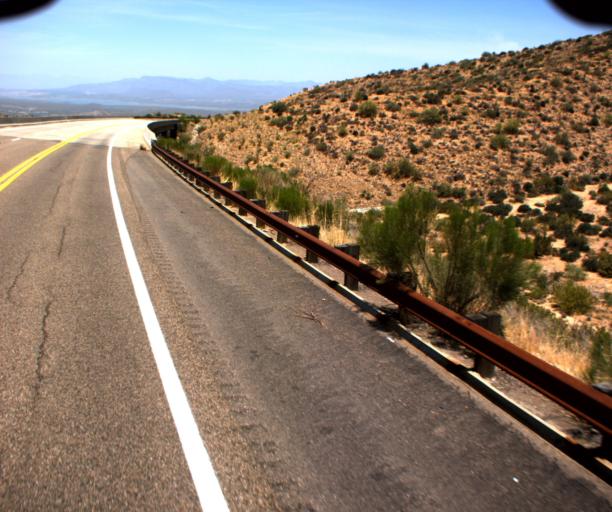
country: US
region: Arizona
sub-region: Gila County
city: Miami
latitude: 33.5494
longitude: -110.9465
